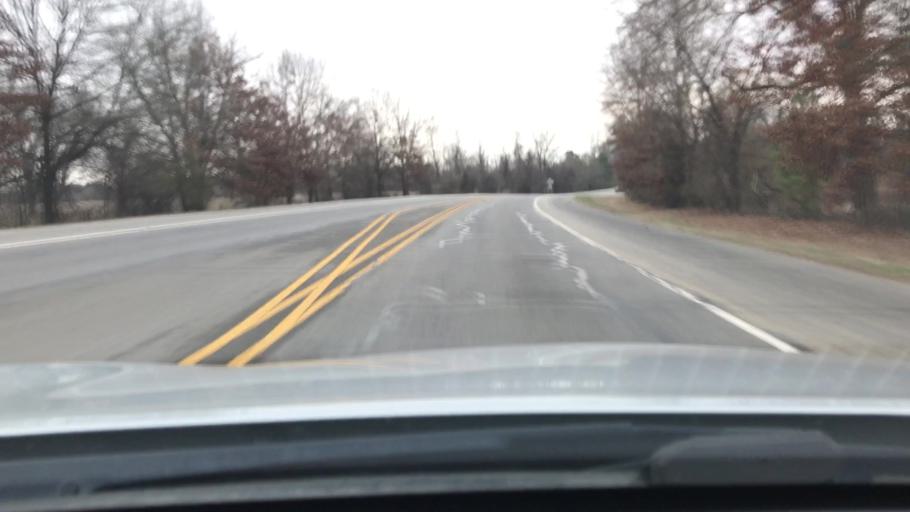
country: US
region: Arkansas
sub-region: Hempstead County
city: Hope
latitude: 33.6865
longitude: -93.5784
